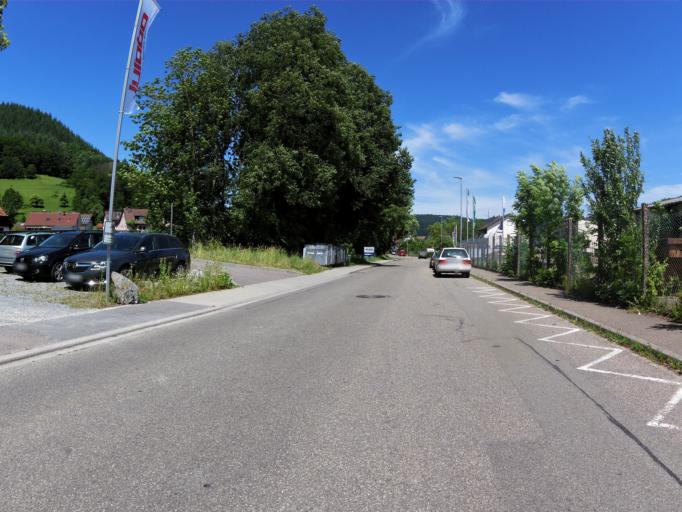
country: DE
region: Baden-Wuerttemberg
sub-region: Freiburg Region
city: Seelbach
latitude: 48.3158
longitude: 7.9364
